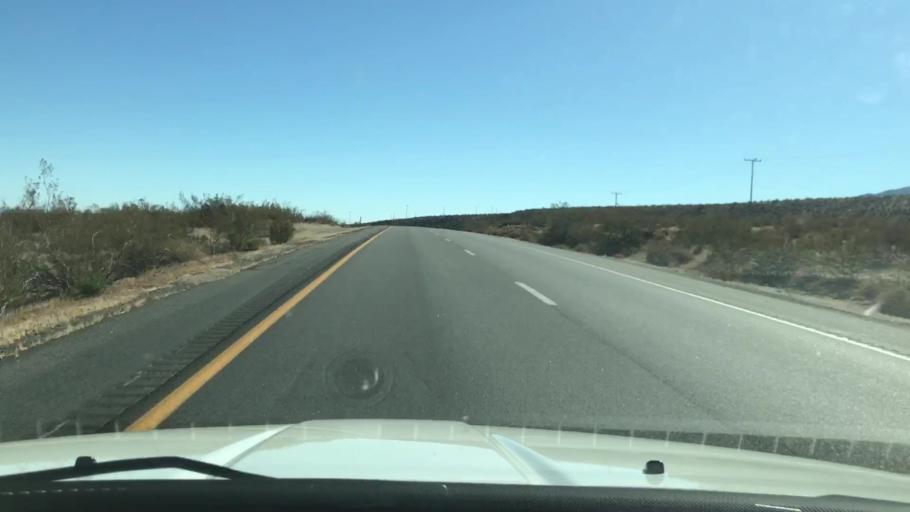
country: US
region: California
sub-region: Kern County
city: Inyokern
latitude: 35.8767
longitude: -117.8893
